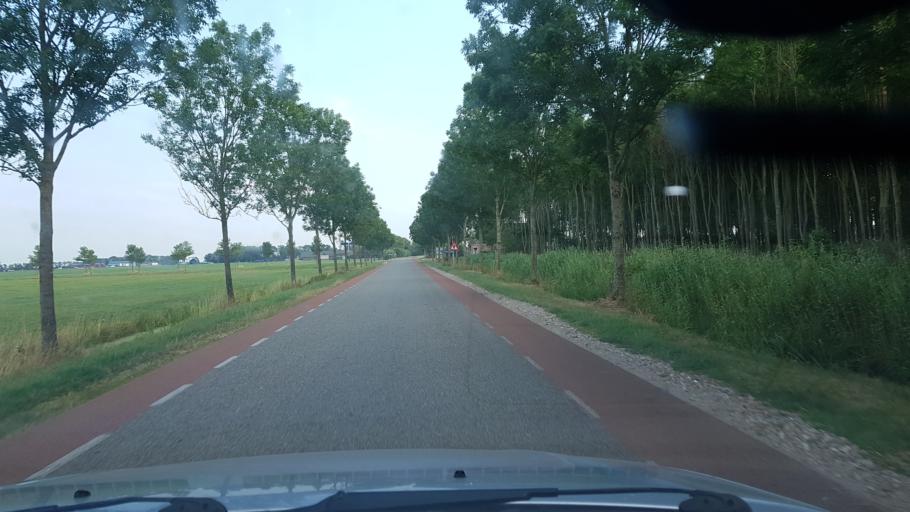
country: NL
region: Friesland
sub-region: Gemeente Ferwerderadiel
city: Burdaard
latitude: 53.3055
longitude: 5.8725
